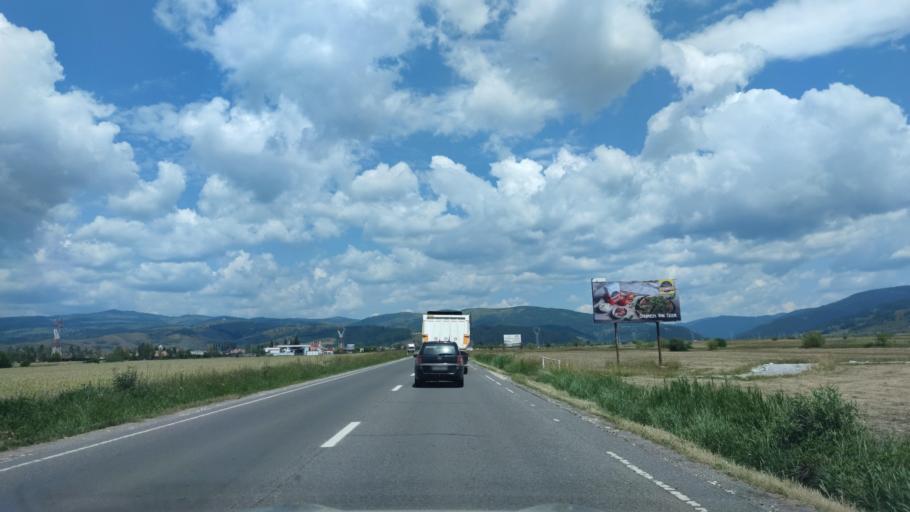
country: RO
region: Harghita
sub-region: Comuna Suseni
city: Valea Stramba
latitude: 46.7085
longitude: 25.6000
